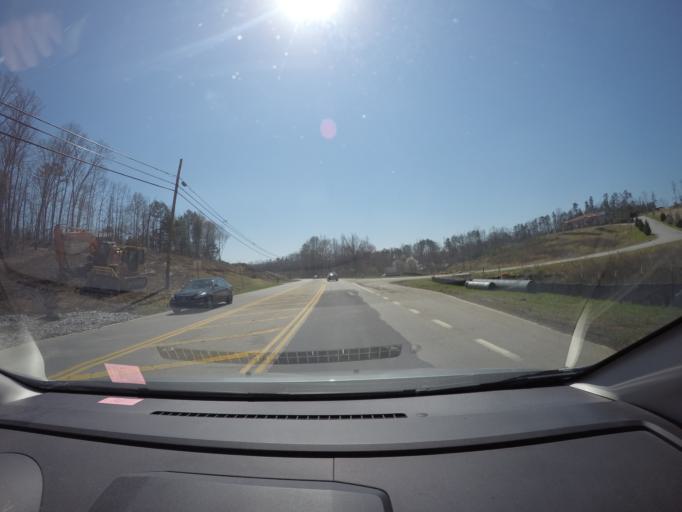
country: US
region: Tennessee
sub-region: Hamilton County
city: Collegedale
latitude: 35.0657
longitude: -85.0812
